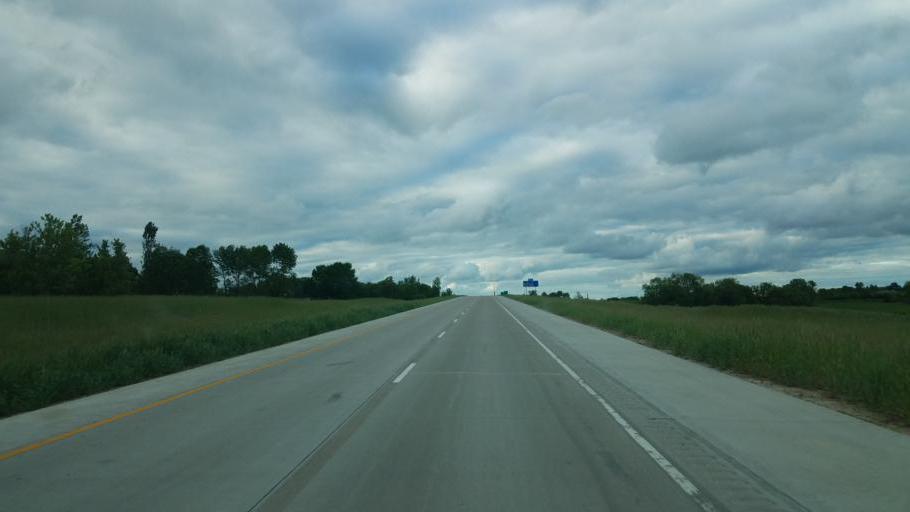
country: US
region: Iowa
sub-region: Decatur County
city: Lamoni
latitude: 40.6145
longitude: -93.8970
